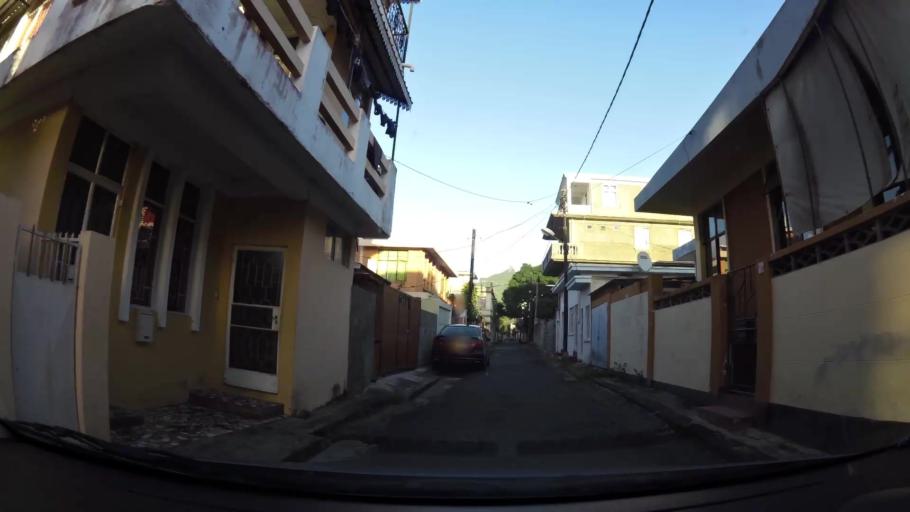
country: MU
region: Port Louis
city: Port Louis
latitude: -20.1685
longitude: 57.4976
